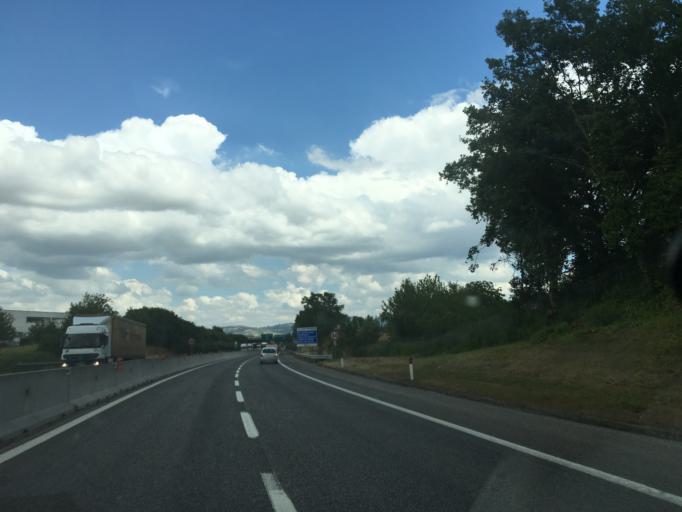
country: IT
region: Campania
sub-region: Provincia di Avellino
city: Grottaminarda
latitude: 41.0630
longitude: 15.0542
